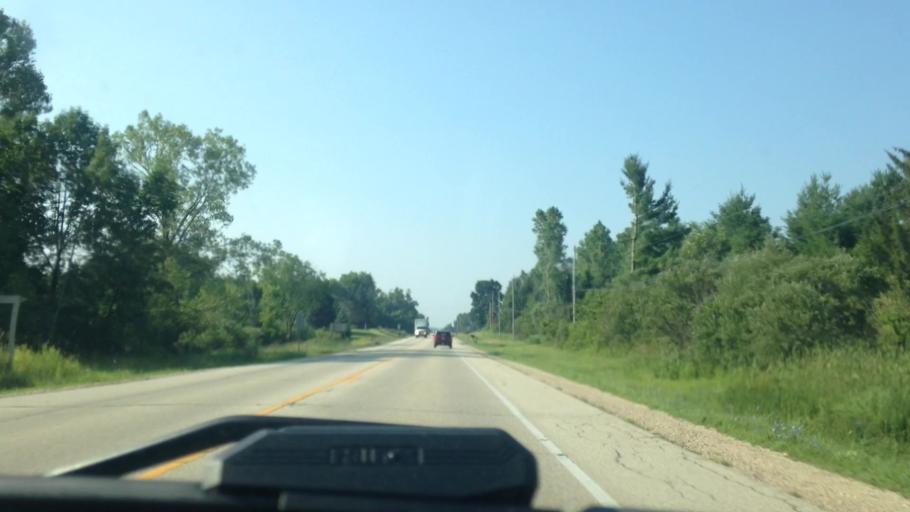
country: US
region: Wisconsin
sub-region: Washington County
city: Slinger
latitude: 43.2949
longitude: -88.2608
